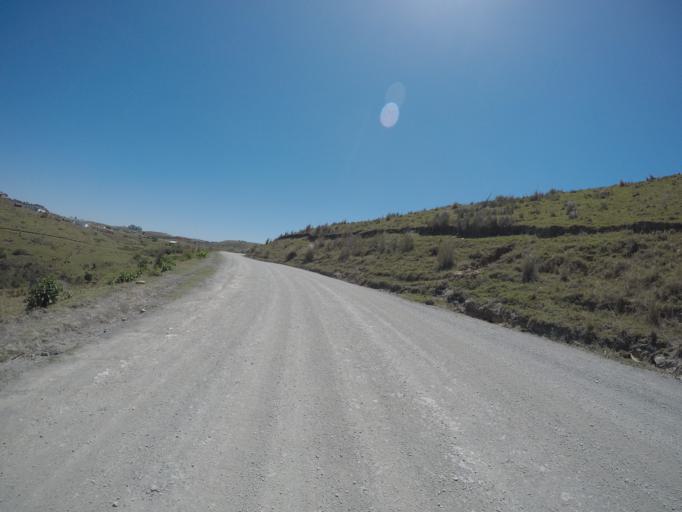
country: ZA
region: Eastern Cape
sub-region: OR Tambo District Municipality
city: Libode
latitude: -31.9963
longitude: 29.0598
